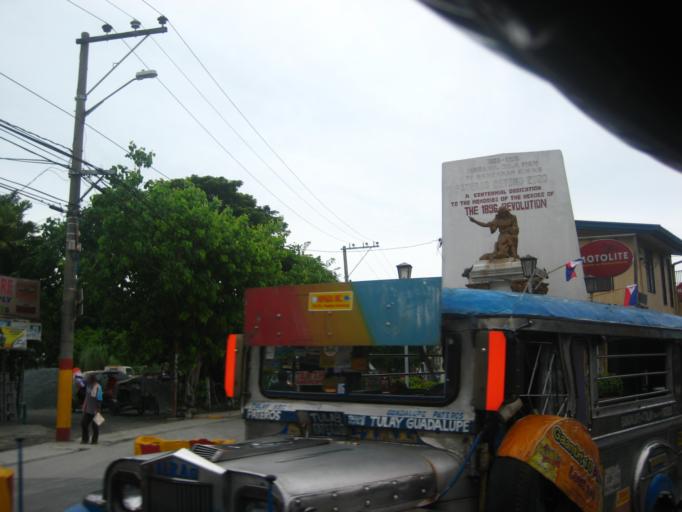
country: PH
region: Calabarzon
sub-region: Province of Rizal
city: Pateros
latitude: 14.5404
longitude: 121.0674
